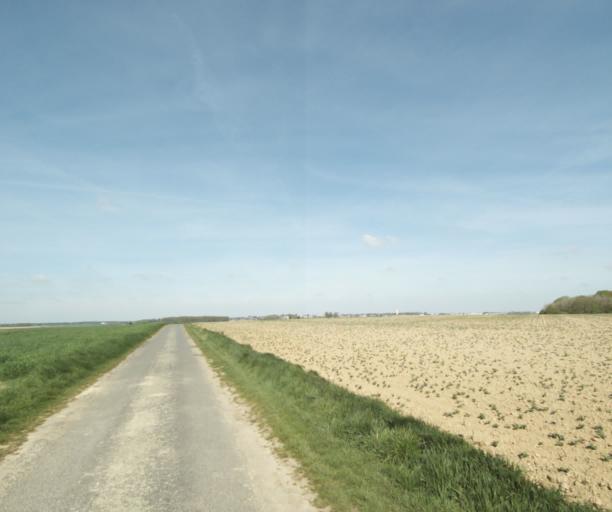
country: FR
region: Ile-de-France
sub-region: Departement de Seine-et-Marne
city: Nangis
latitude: 48.5351
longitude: 3.0408
